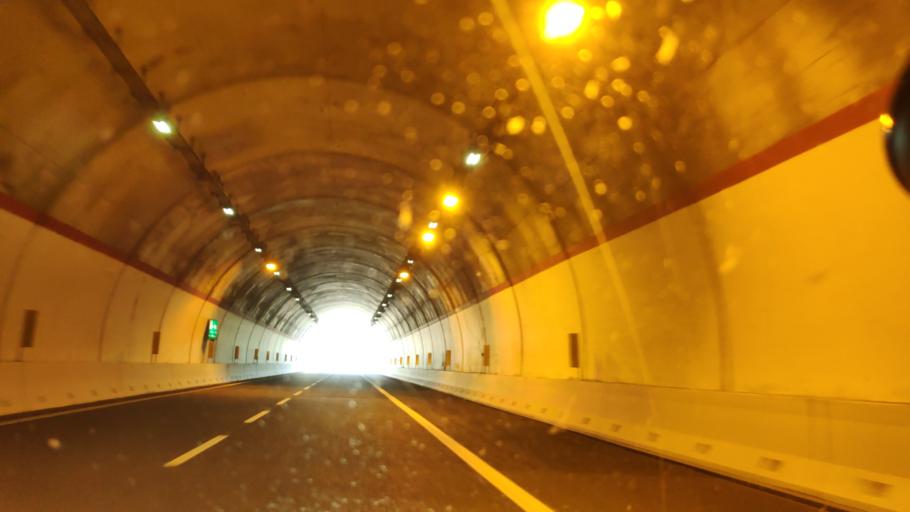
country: IT
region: Campania
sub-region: Provincia di Salerno
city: Casalbuono
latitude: 40.2325
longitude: 15.6655
